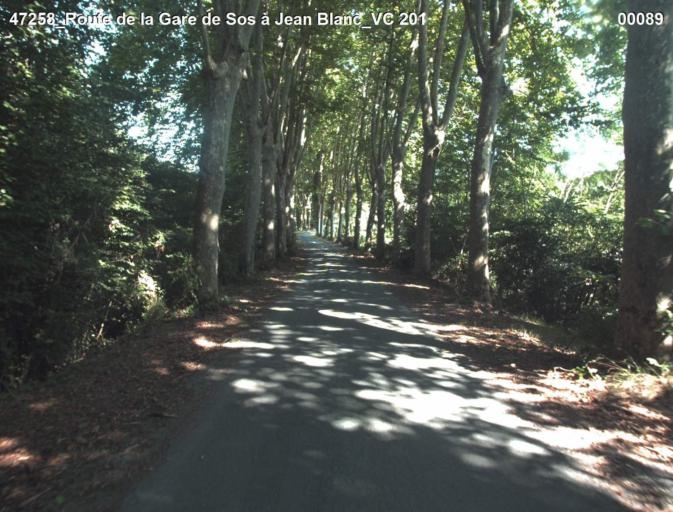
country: FR
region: Midi-Pyrenees
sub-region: Departement du Gers
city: Montreal
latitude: 44.0390
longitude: 0.1443
